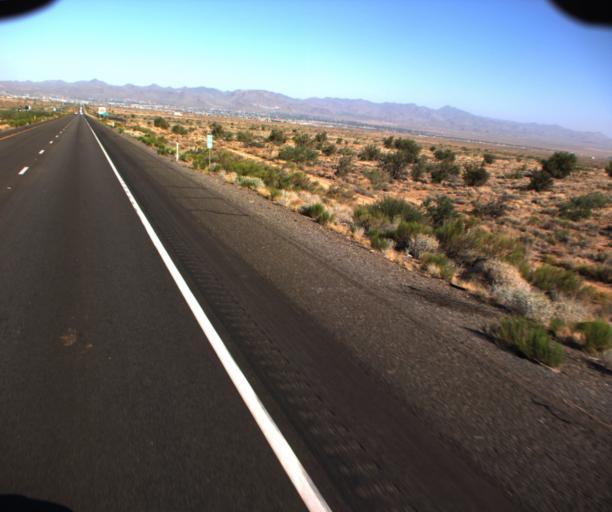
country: US
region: Arizona
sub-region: Mohave County
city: New Kingman-Butler
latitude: 35.2026
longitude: -113.9339
